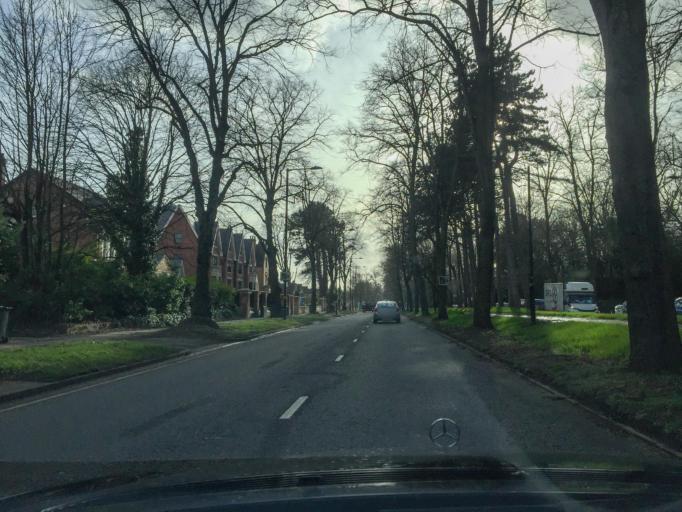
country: GB
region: England
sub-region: City and Borough of Birmingham
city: Birmingham
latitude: 52.4523
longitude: -1.9141
